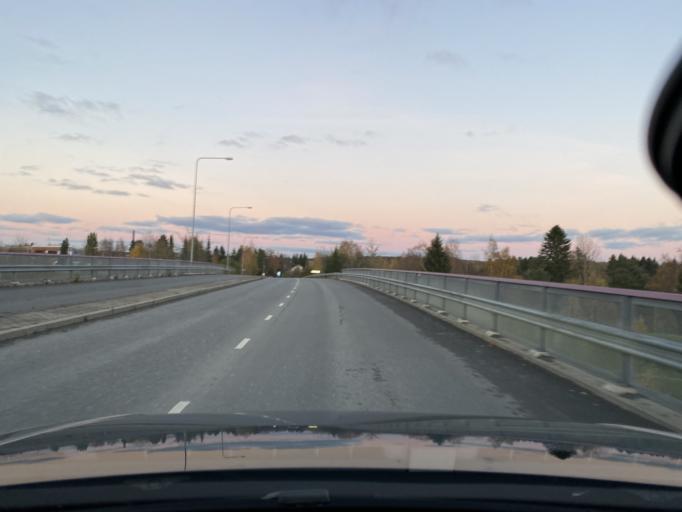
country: FI
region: Pirkanmaa
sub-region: Tampere
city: Lempaeaelae
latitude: 61.3270
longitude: 23.7583
